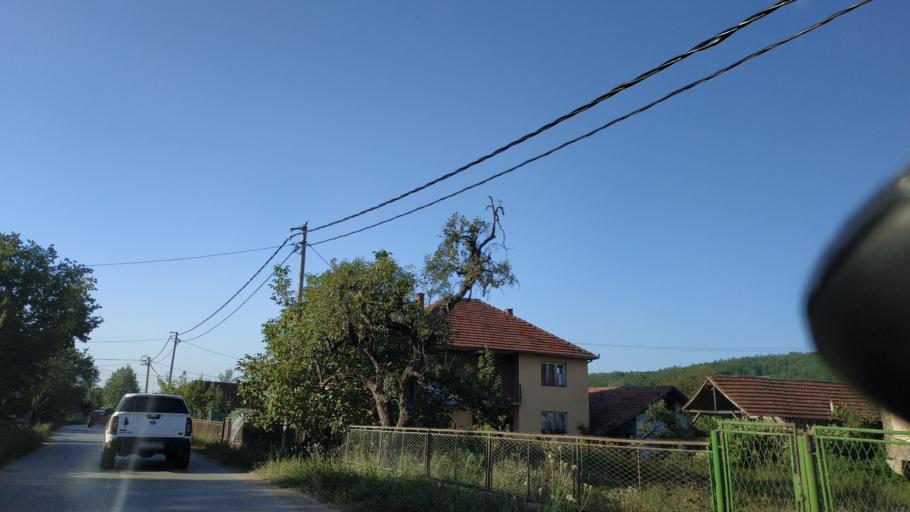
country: RS
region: Central Serbia
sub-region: Rasinski Okrug
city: Krusevac
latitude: 43.4897
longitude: 21.3465
